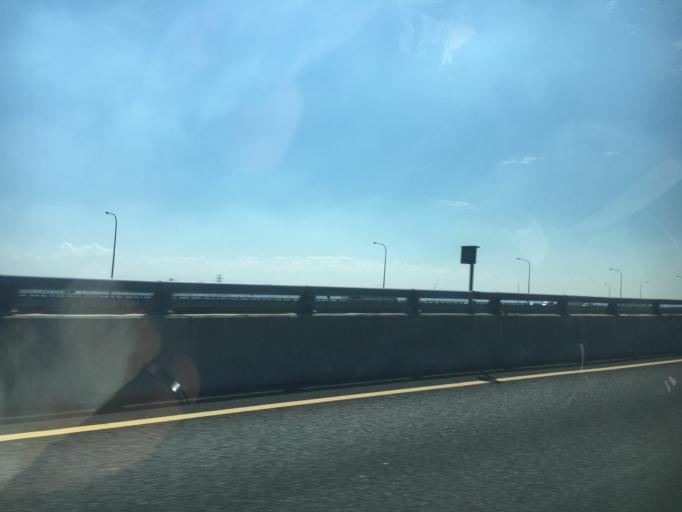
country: TW
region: Taiwan
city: Taoyuan City
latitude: 25.0218
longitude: 121.2762
